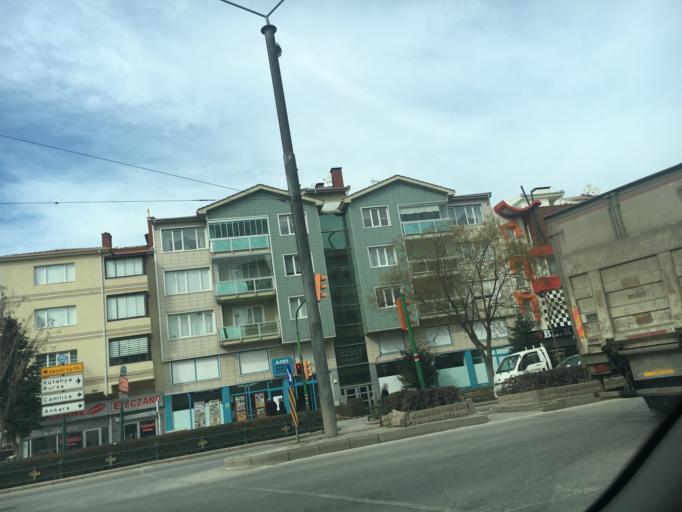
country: TR
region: Eskisehir
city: Eskisehir
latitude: 39.7674
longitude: 30.5012
